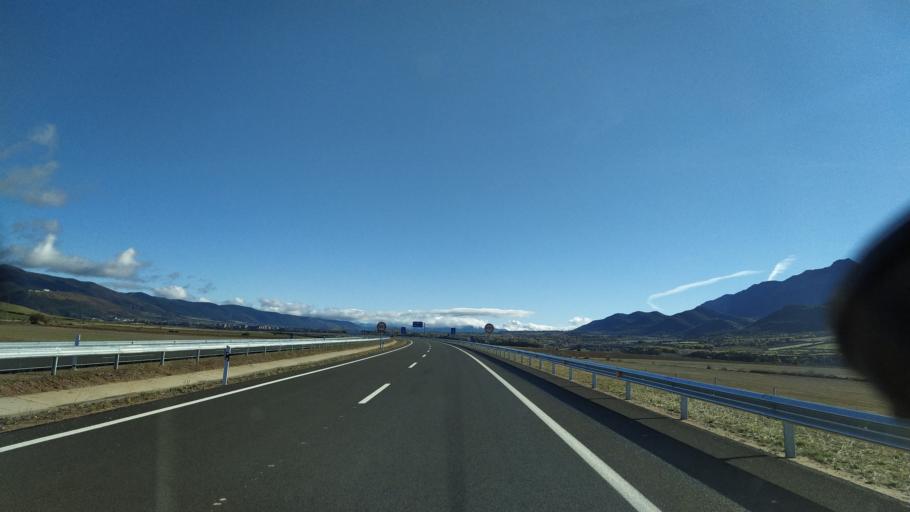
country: ES
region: Aragon
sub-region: Provincia de Huesca
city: Jaca
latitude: 42.5629
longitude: -0.6174
